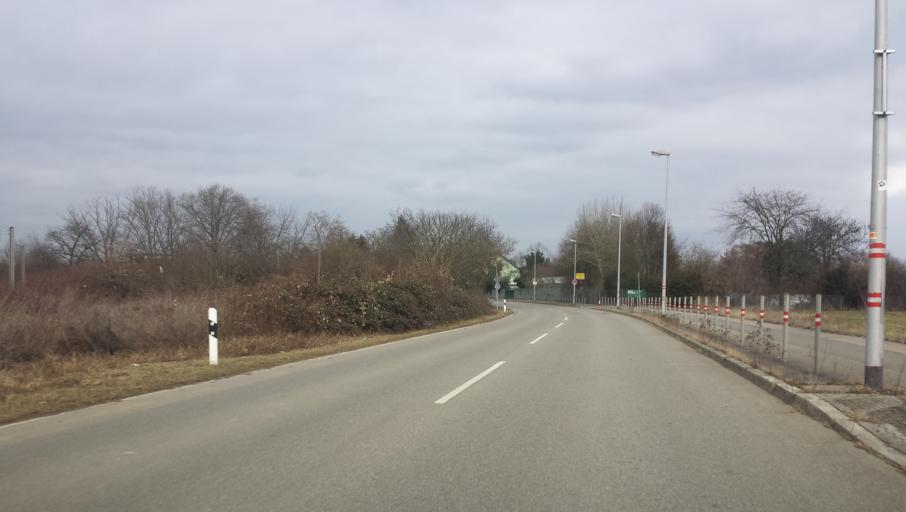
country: DE
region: Baden-Wuerttemberg
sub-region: Karlsruhe Region
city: Ilvesheim
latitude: 49.4721
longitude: 8.5244
